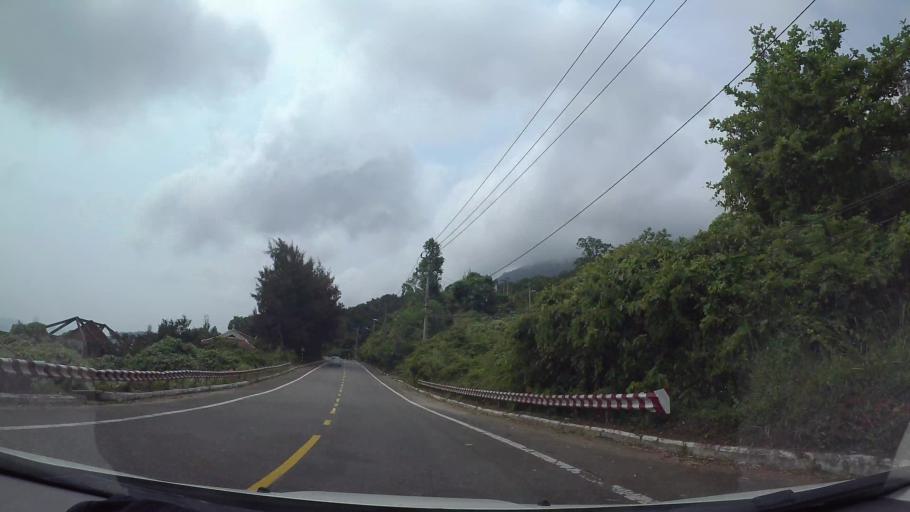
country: VN
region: Da Nang
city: Son Tra
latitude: 16.1064
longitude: 108.2988
